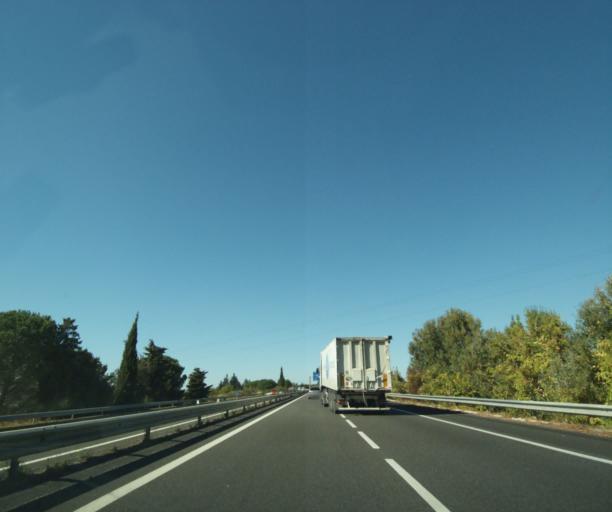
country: FR
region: Languedoc-Roussillon
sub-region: Departement du Gard
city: Caissargues
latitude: 43.8012
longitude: 4.3810
